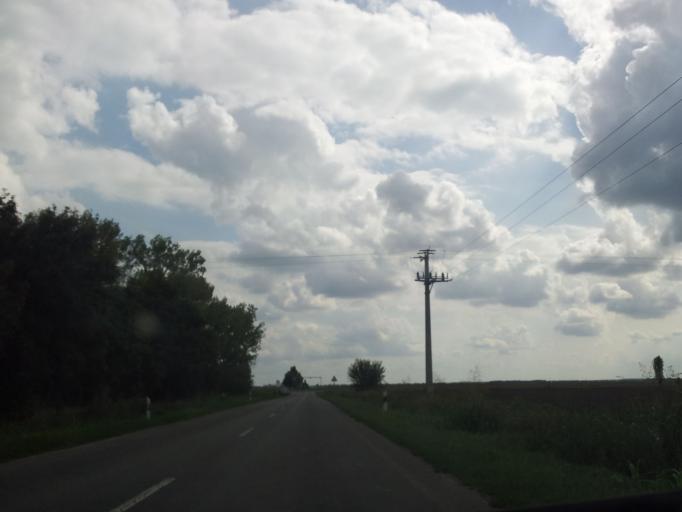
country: HU
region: Baranya
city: Mohacs
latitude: 45.9744
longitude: 18.6749
